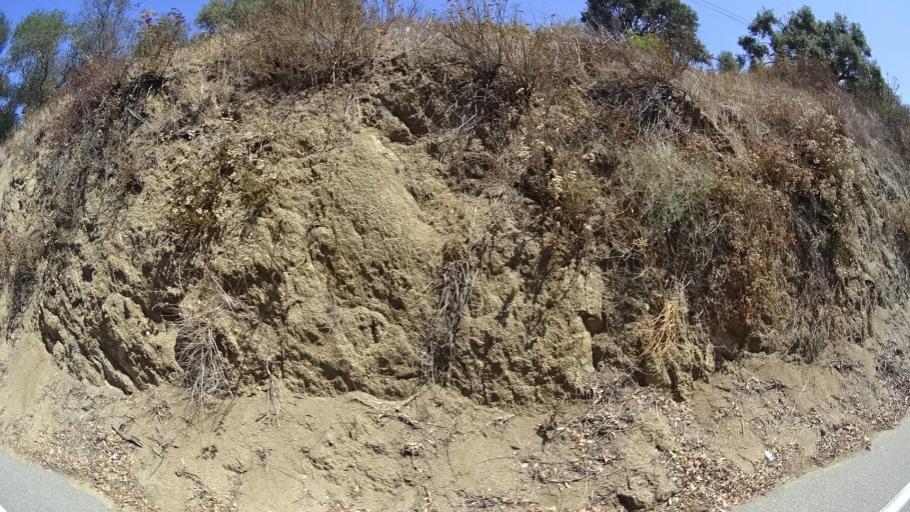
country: US
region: California
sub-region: San Diego County
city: Fallbrook
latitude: 33.3469
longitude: -117.1943
